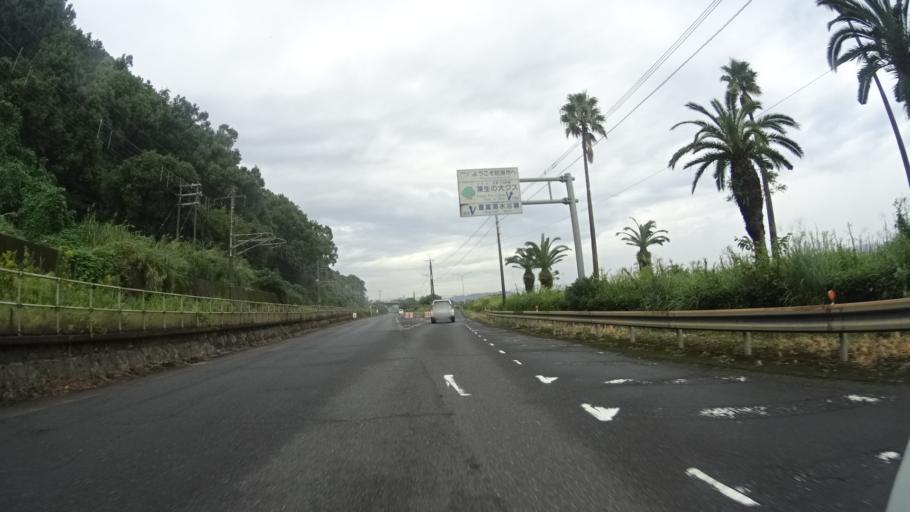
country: JP
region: Kagoshima
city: Kajiki
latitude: 31.6946
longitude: 130.6142
